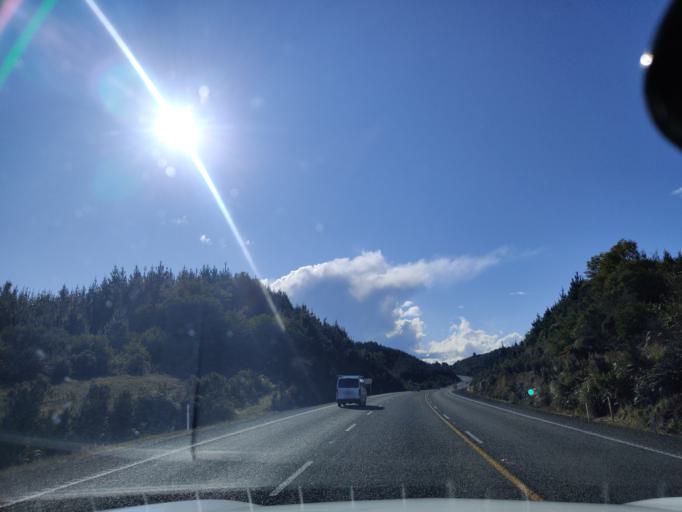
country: NZ
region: Waikato
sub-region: South Waikato District
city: Tokoroa
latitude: -38.3100
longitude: 175.9708
